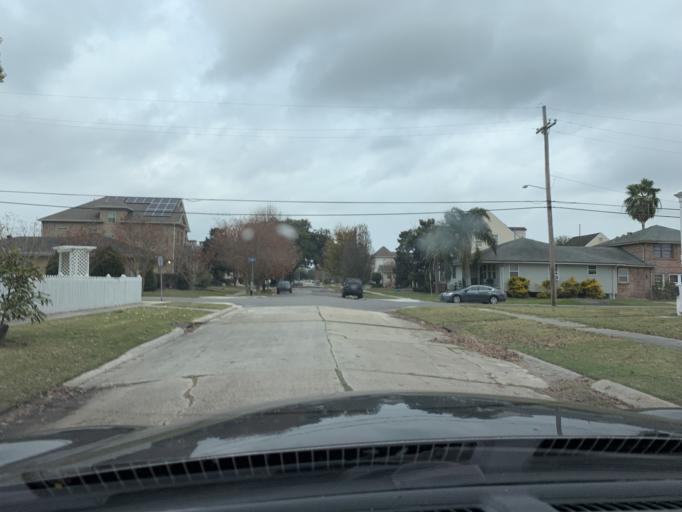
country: US
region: Louisiana
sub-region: Jefferson Parish
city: Metairie
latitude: 30.0079
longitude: -90.1034
